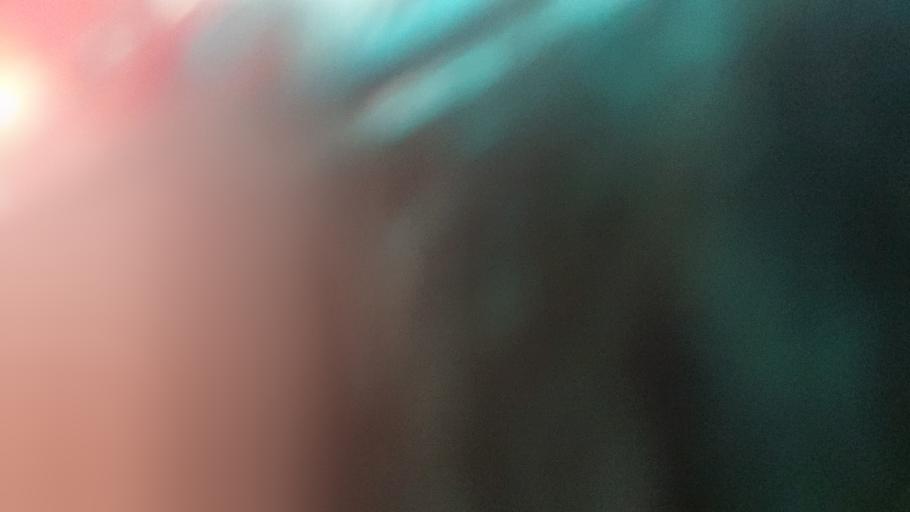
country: TW
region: Taiwan
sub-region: Chiayi
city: Taibao
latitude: 23.7073
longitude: 120.1827
